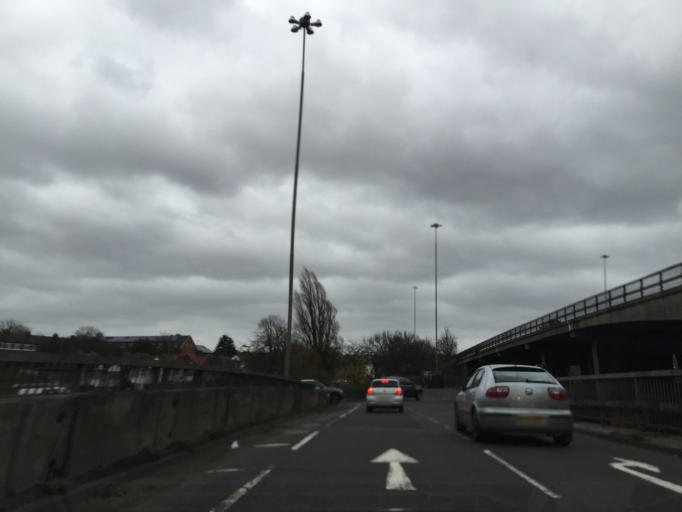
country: GB
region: England
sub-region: Greater London
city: Hendon
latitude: 51.5771
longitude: -0.2183
